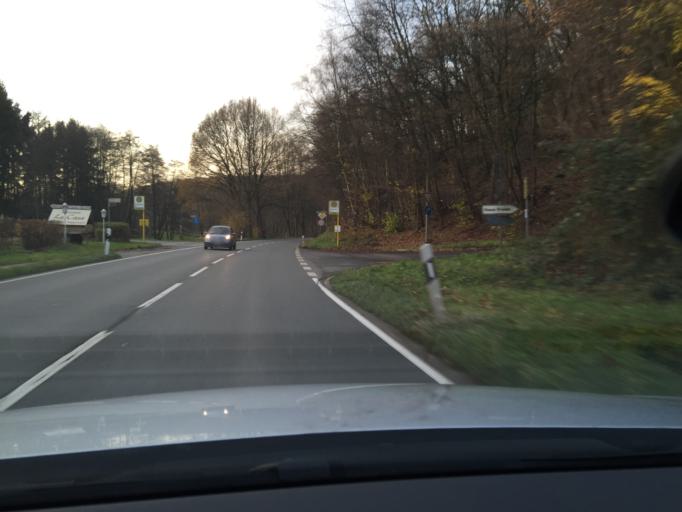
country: DE
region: North Rhine-Westphalia
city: Hattingen
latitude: 51.3703
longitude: 7.1826
